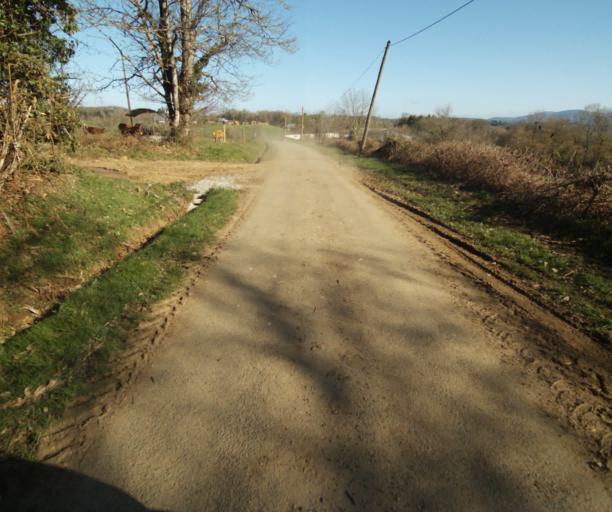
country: FR
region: Limousin
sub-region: Departement de la Correze
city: Seilhac
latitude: 45.3785
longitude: 1.7644
